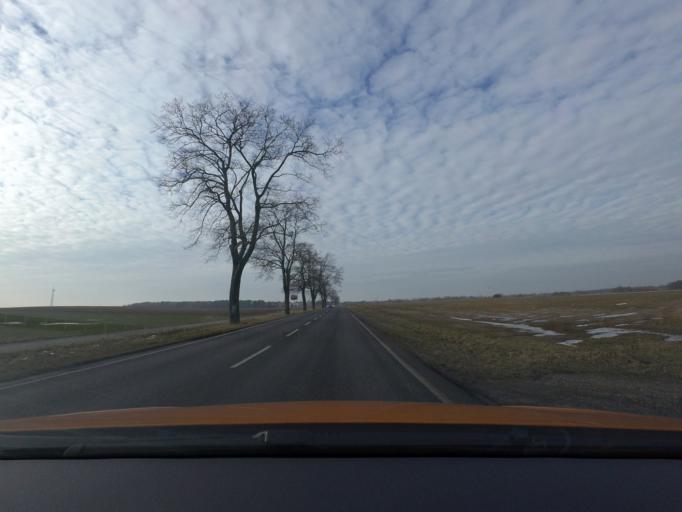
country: DE
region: Brandenburg
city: Gransee
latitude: 52.8990
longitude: 13.1798
